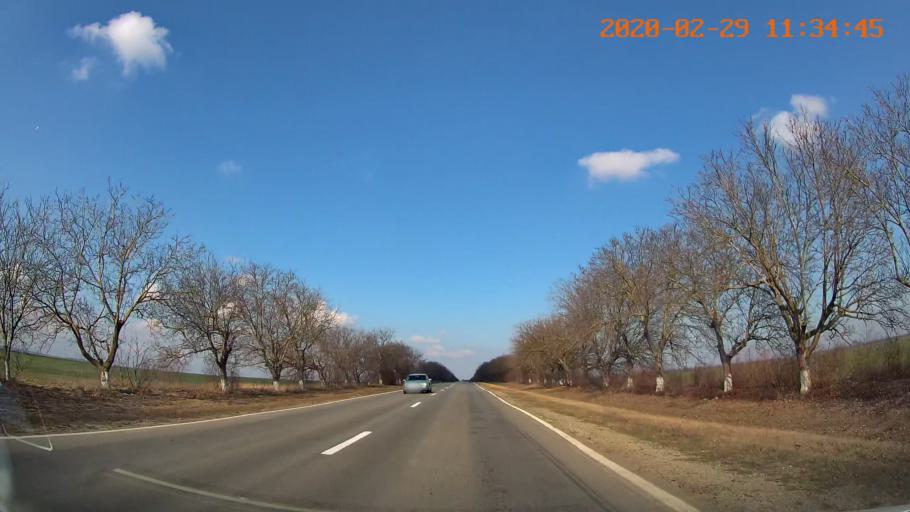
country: MD
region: Rezina
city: Saharna
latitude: 47.5703
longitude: 29.0704
